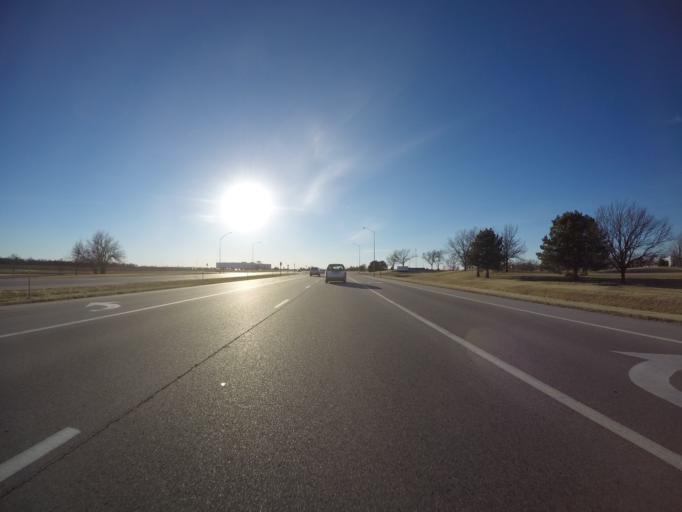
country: US
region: Kansas
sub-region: Sedgwick County
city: Wichita
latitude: 37.6374
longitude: -97.4189
